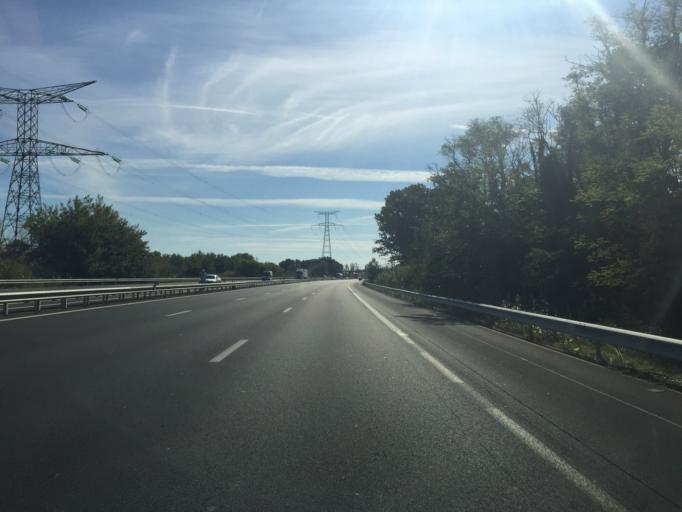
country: FR
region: Provence-Alpes-Cote d'Azur
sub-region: Departement des Bouches-du-Rhone
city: Cabannes
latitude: 43.8537
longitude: 4.9837
